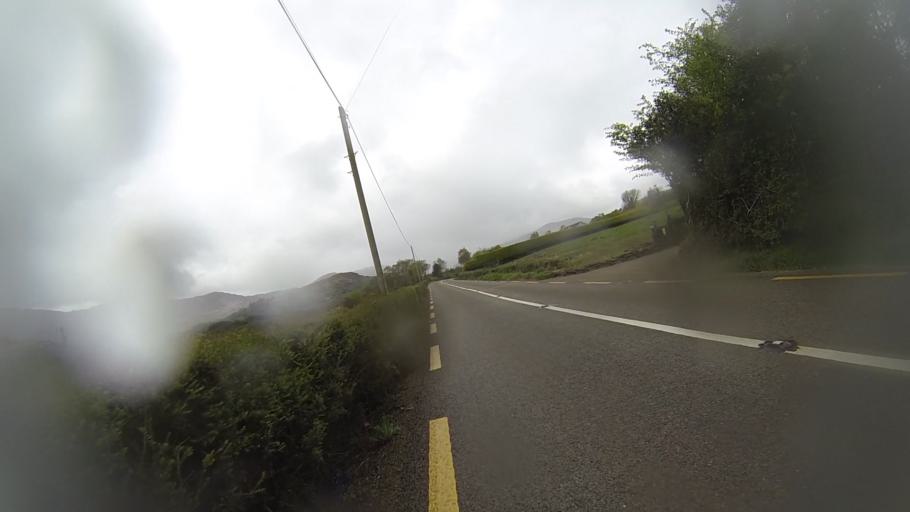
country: IE
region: Munster
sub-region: Ciarrai
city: Kenmare
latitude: 51.8138
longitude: -9.5439
